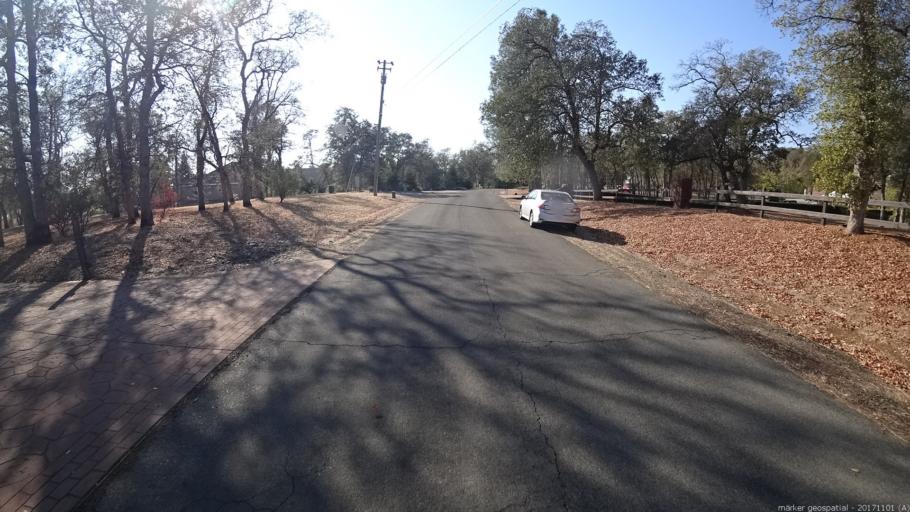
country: US
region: California
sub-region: Shasta County
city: Shasta Lake
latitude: 40.6744
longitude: -122.3408
